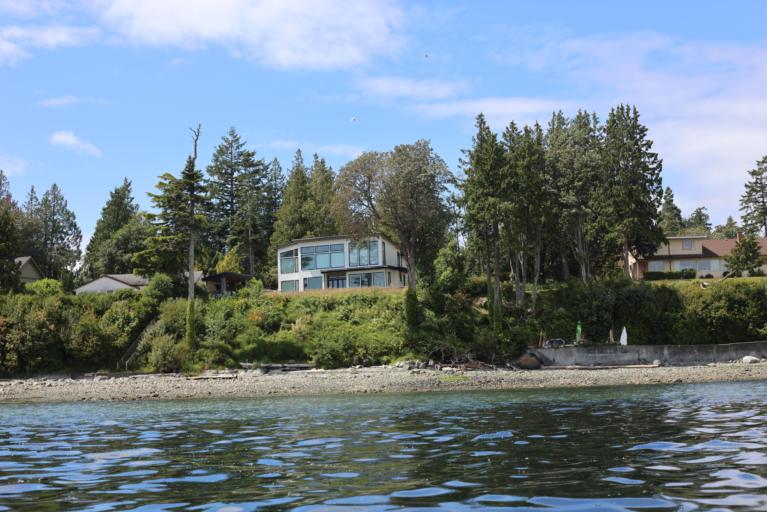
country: CA
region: British Columbia
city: North Saanich
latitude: 48.6125
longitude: -123.3969
